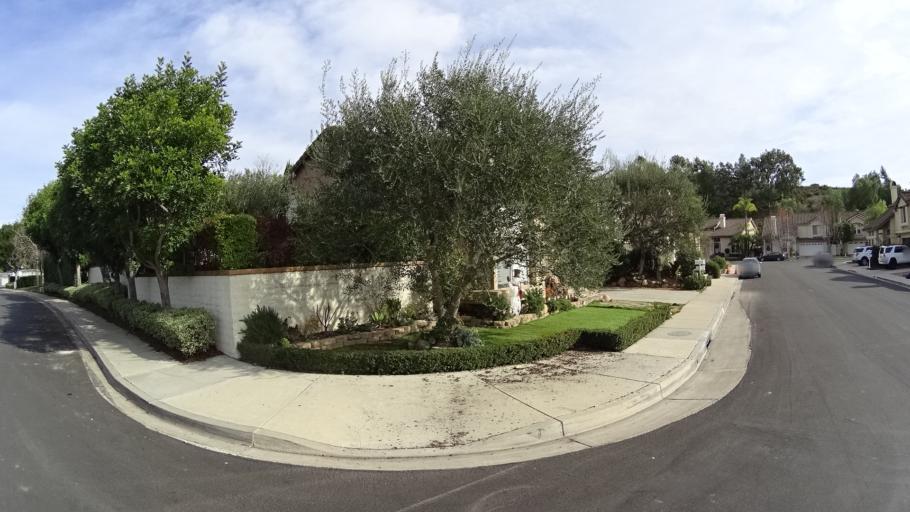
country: US
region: California
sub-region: Orange County
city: Laguna Woods
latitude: 33.5932
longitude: -117.7476
